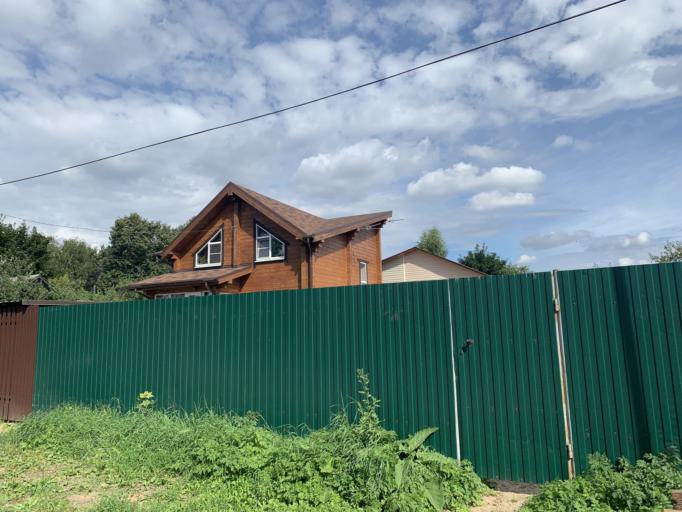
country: RU
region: Moskovskaya
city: Mamontovka
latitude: 55.9865
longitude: 37.8035
